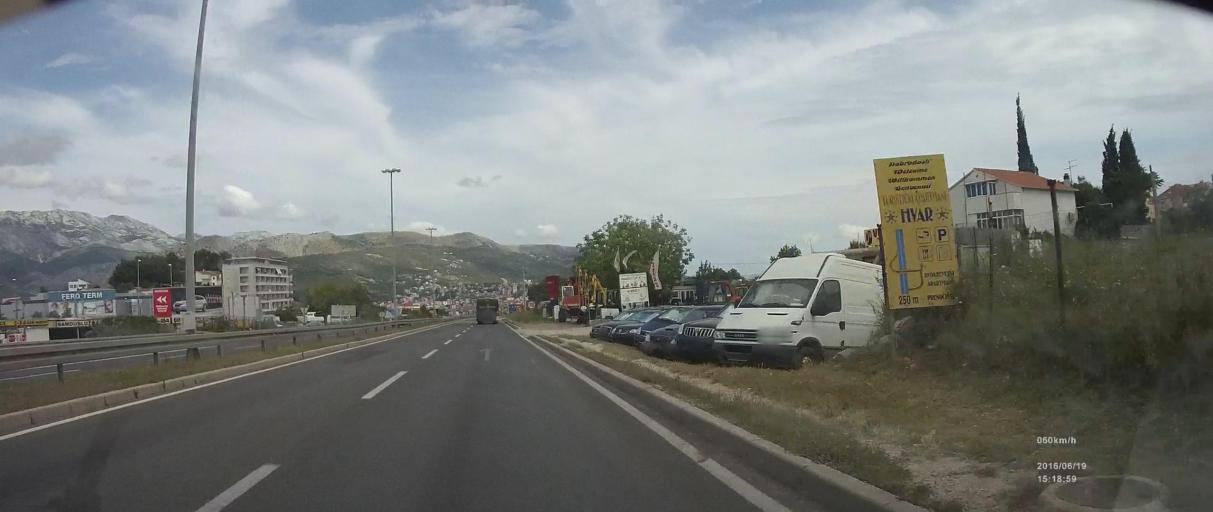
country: HR
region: Splitsko-Dalmatinska
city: Kamen
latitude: 43.5079
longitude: 16.4999
